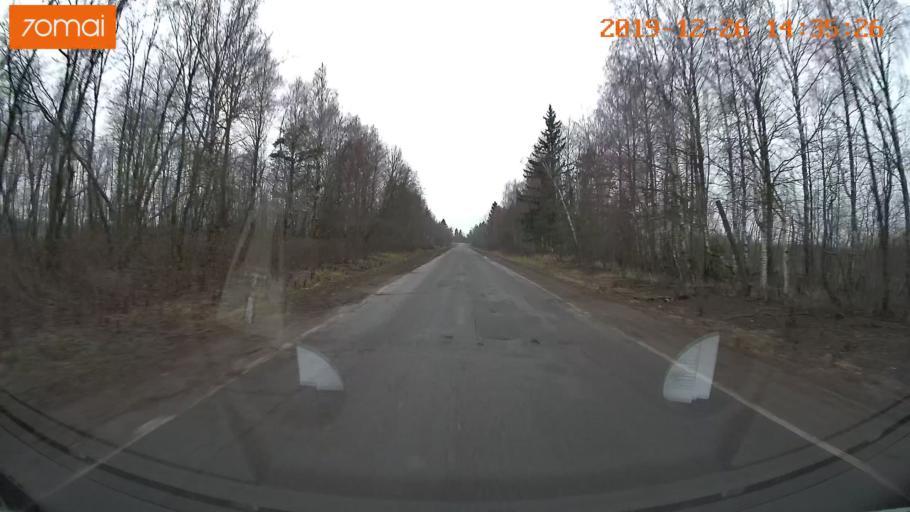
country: RU
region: Jaroslavl
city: Poshekhon'ye
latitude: 58.4204
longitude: 38.9847
